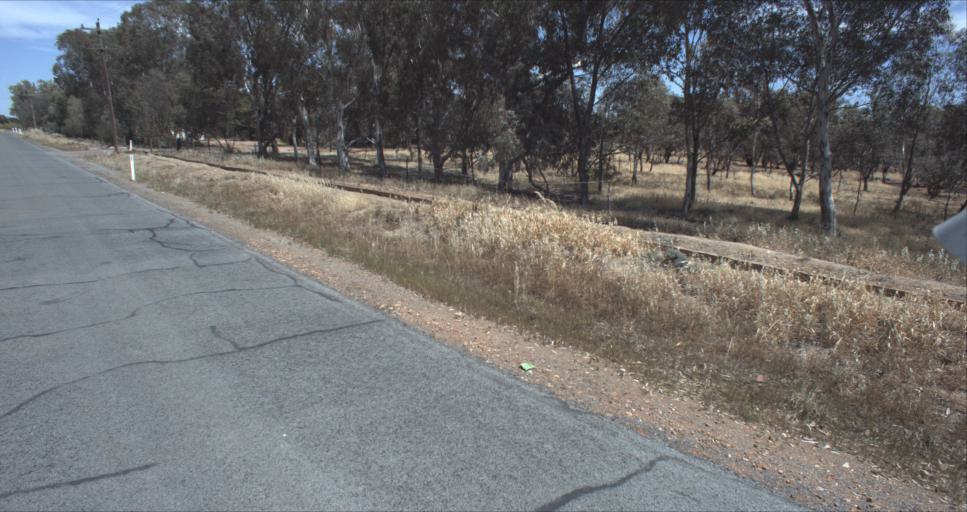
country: AU
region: New South Wales
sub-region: Leeton
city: Leeton
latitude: -34.5803
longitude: 146.4282
